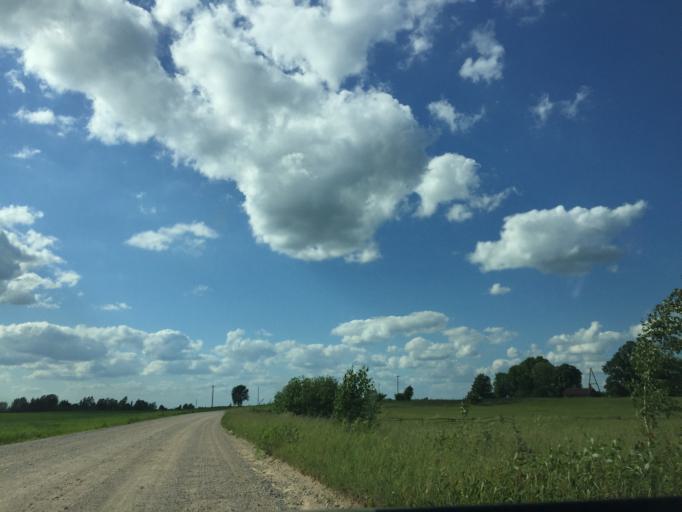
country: LV
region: Jaunpils
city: Jaunpils
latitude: 56.8129
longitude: 23.0746
